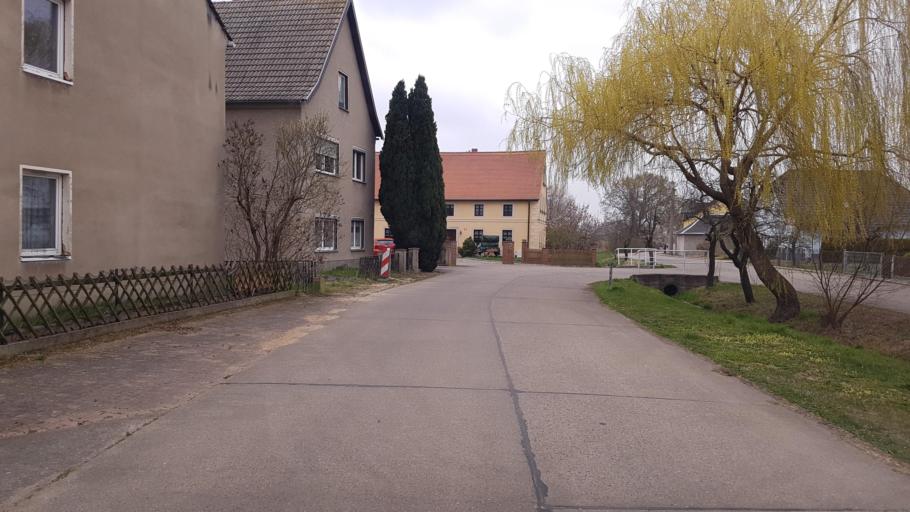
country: DE
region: Saxony
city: Nauwalde
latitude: 51.4223
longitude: 13.3877
